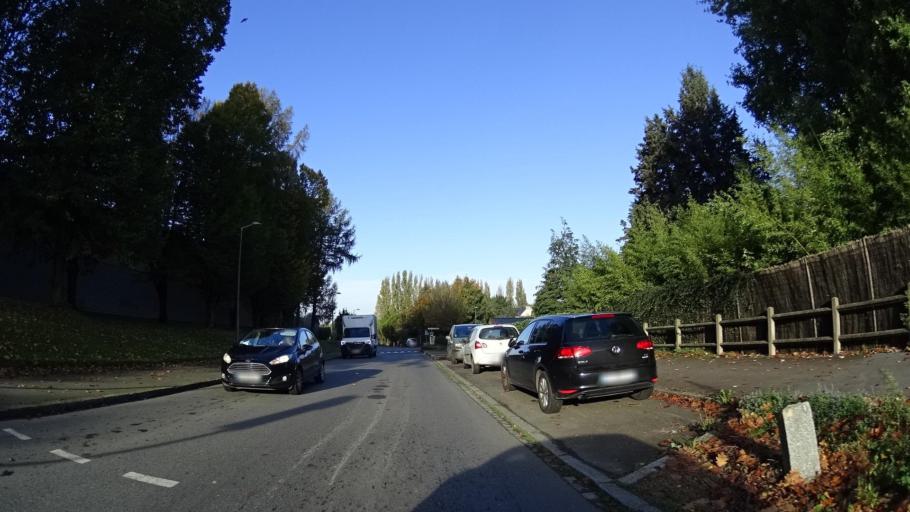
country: FR
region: Brittany
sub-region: Departement d'Ille-et-Vilaine
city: Saint-Gregoire
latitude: 48.1544
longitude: -1.6921
